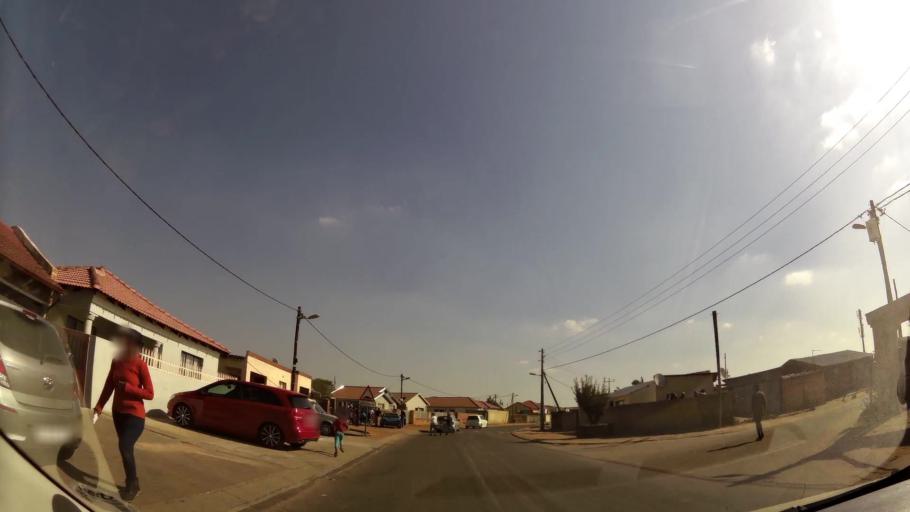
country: ZA
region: Gauteng
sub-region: City of Johannesburg Metropolitan Municipality
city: Roodepoort
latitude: -26.1604
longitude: 27.7988
